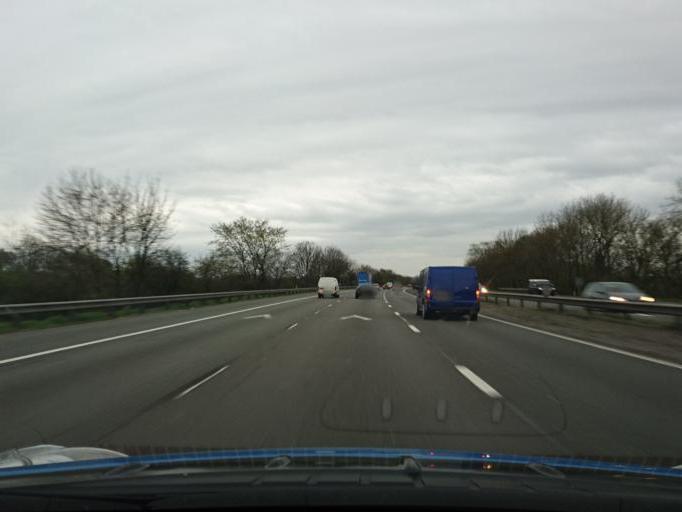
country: GB
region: England
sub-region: Staffordshire
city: Barlaston
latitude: 52.9146
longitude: -2.1960
